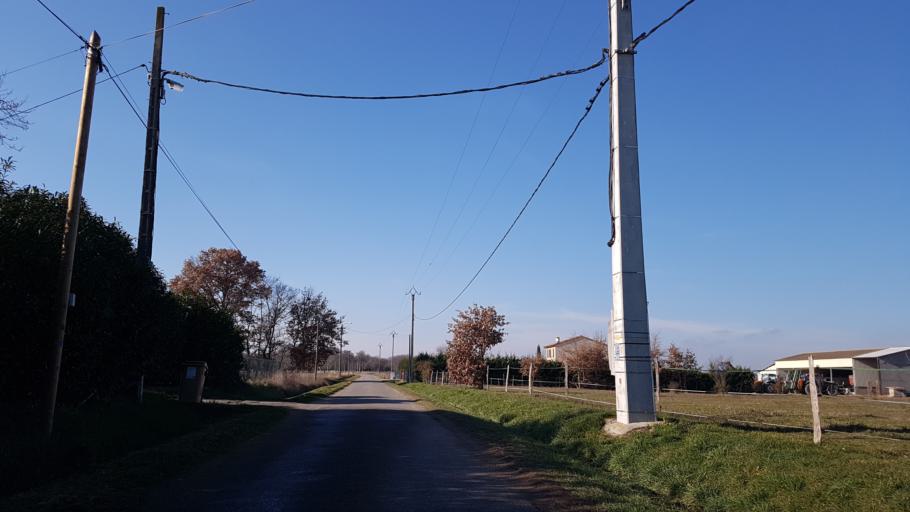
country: FR
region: Midi-Pyrenees
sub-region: Departement de l'Ariege
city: La Tour-du-Crieu
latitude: 43.1632
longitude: 1.6780
